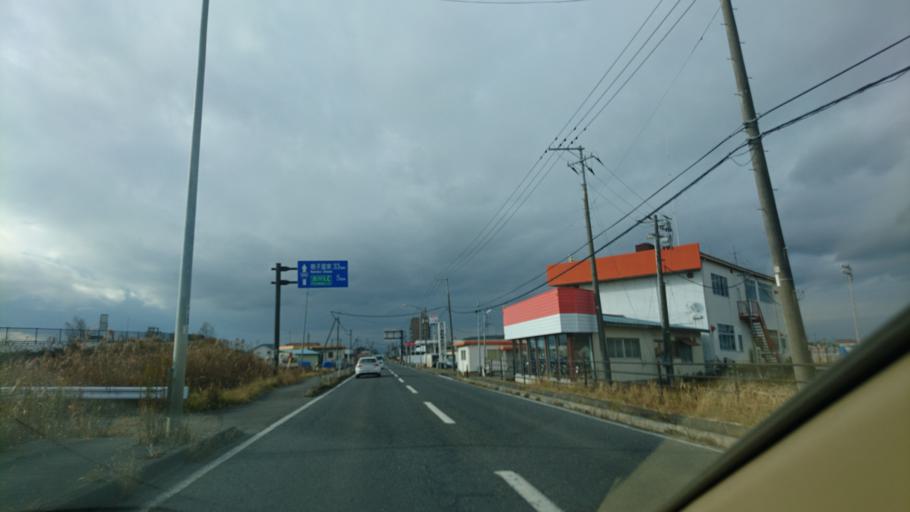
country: JP
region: Miyagi
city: Furukawa
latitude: 38.5690
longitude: 140.9893
